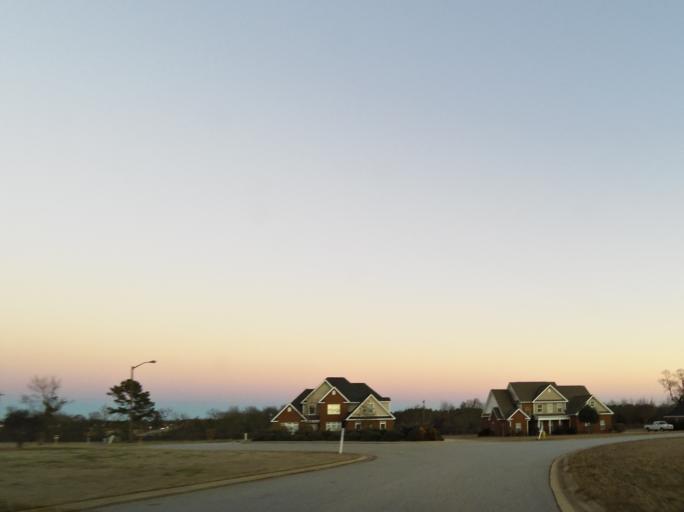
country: US
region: Georgia
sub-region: Peach County
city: Byron
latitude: 32.6055
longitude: -83.7691
